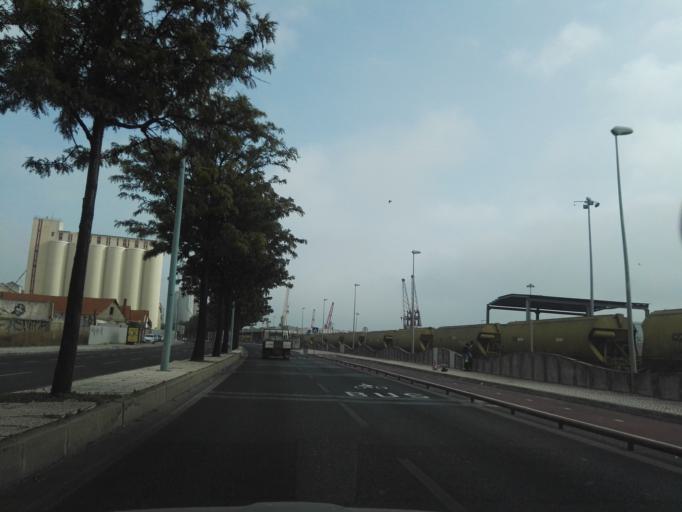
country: PT
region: Lisbon
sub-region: Lisbon
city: Lisbon
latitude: 38.7284
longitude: -9.1077
